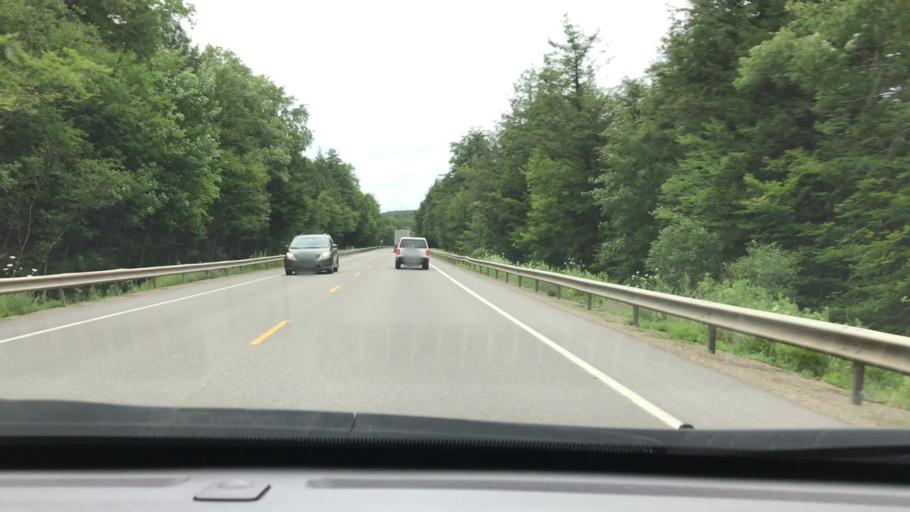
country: US
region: Pennsylvania
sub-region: McKean County
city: Kane
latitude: 41.6820
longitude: -78.6875
